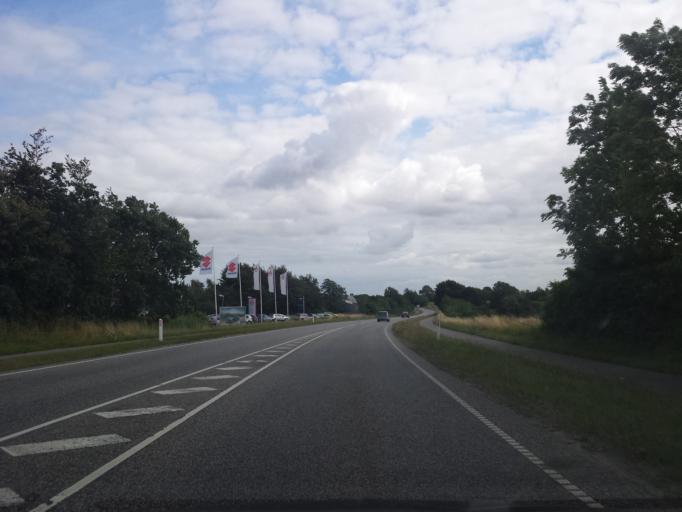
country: DK
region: South Denmark
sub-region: Sonderborg Kommune
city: Guderup
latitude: 54.9944
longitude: 9.8569
